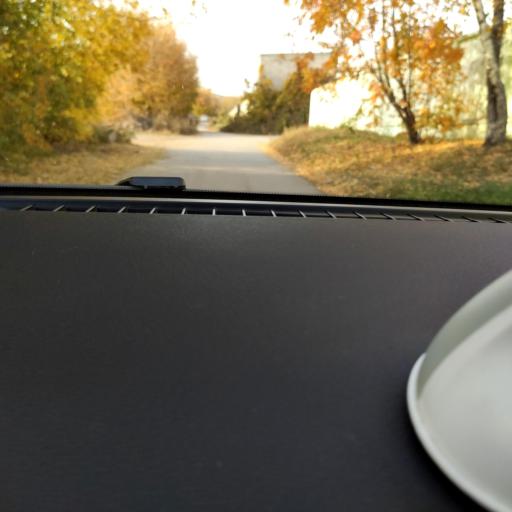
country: RU
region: Samara
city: Samara
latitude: 53.2263
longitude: 50.2242
